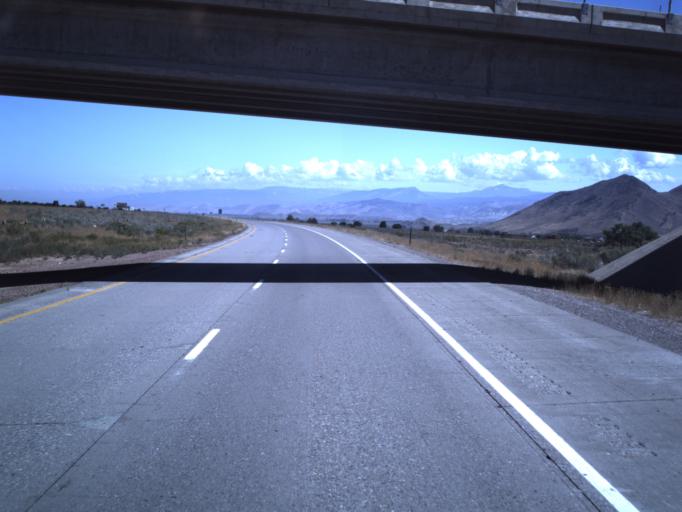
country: US
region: Utah
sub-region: Sevier County
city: Aurora
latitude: 38.8599
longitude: -111.9845
